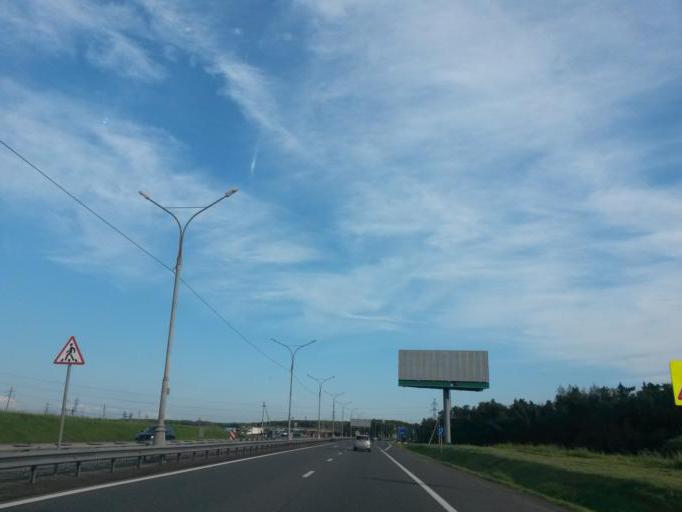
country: RU
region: Moskovskaya
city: Gorki-Leninskiye
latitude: 55.4896
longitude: 37.8479
